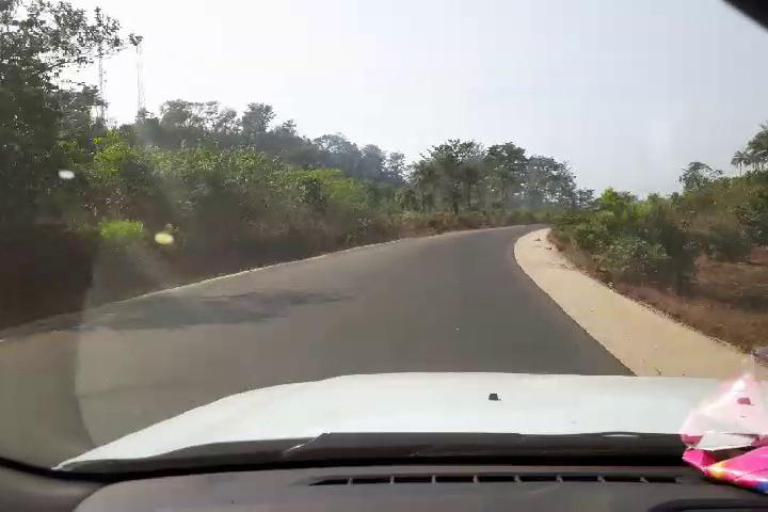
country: SL
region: Western Area
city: Waterloo
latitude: 8.2641
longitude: -13.1610
